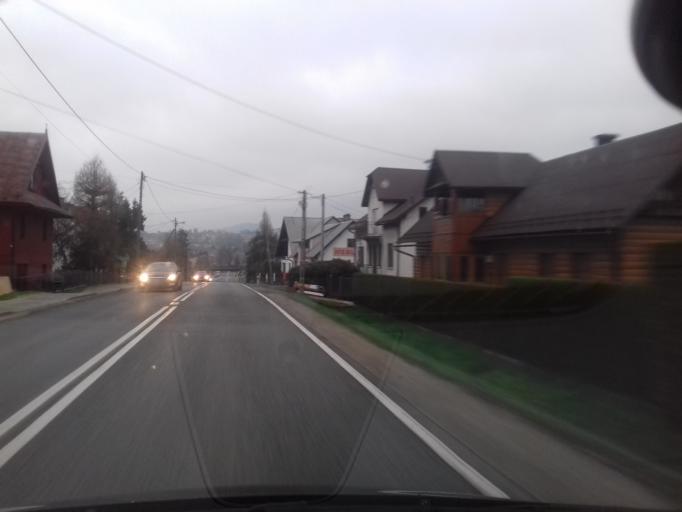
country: PL
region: Lesser Poland Voivodeship
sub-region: Powiat limanowski
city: Mszana Dolna
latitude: 49.6784
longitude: 20.0872
